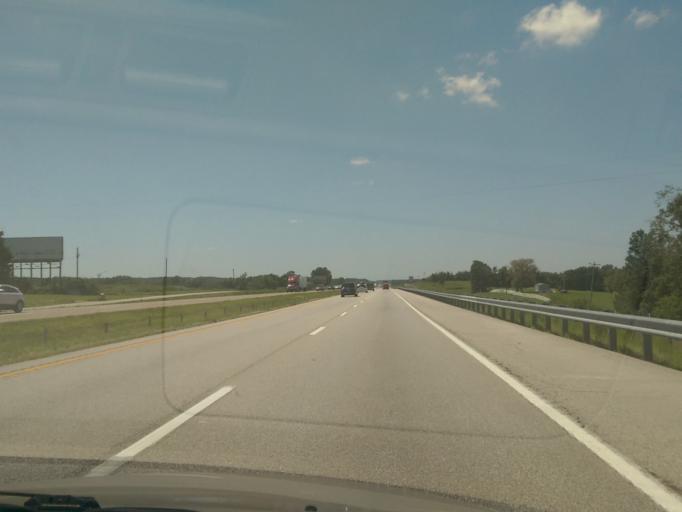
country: US
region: Missouri
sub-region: Cooper County
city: Boonville
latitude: 38.9353
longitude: -92.8534
